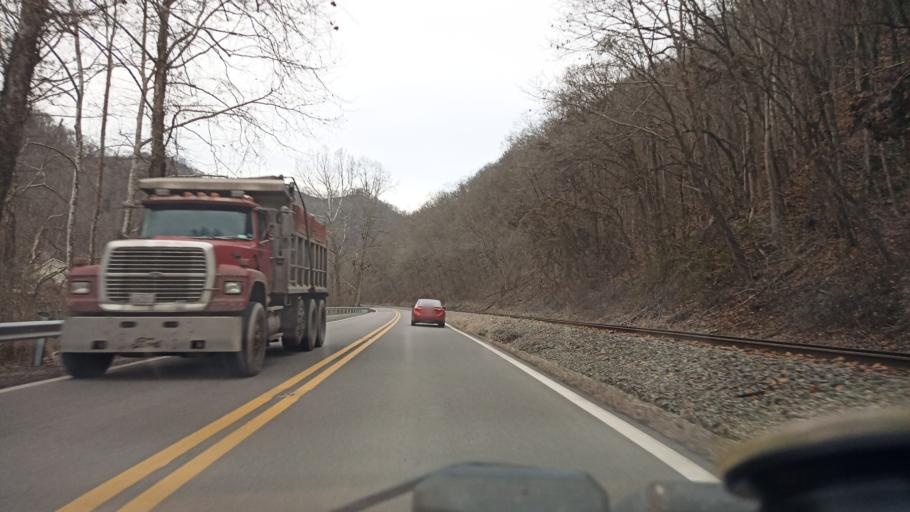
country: US
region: West Virginia
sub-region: Logan County
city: Mallory
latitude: 37.7204
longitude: -81.8698
